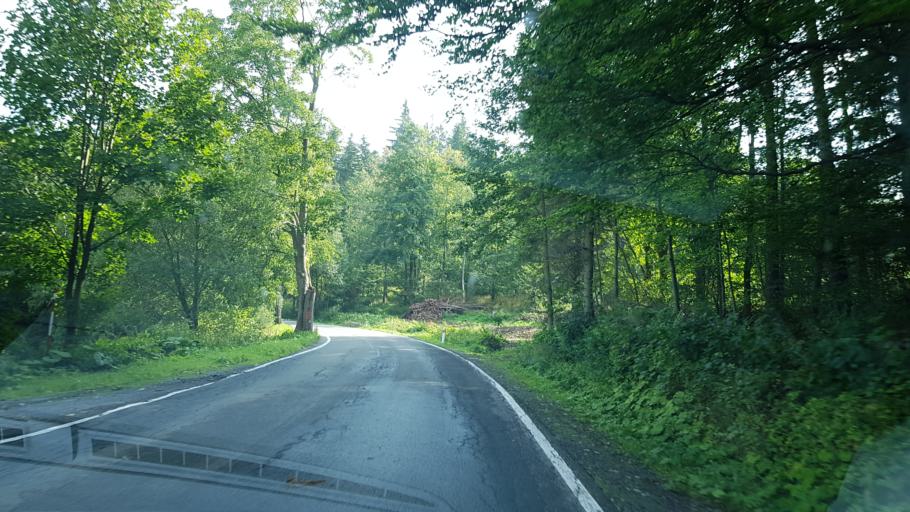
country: CZ
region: Olomoucky
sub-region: Okres Jesenik
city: Jesenik
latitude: 50.2111
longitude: 17.2442
